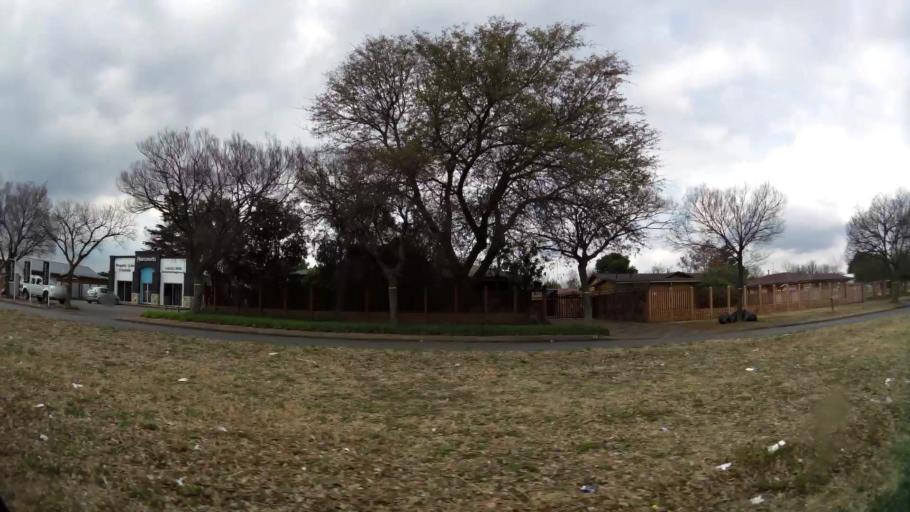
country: ZA
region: Gauteng
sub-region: Sedibeng District Municipality
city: Vanderbijlpark
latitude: -26.7181
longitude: 27.8239
